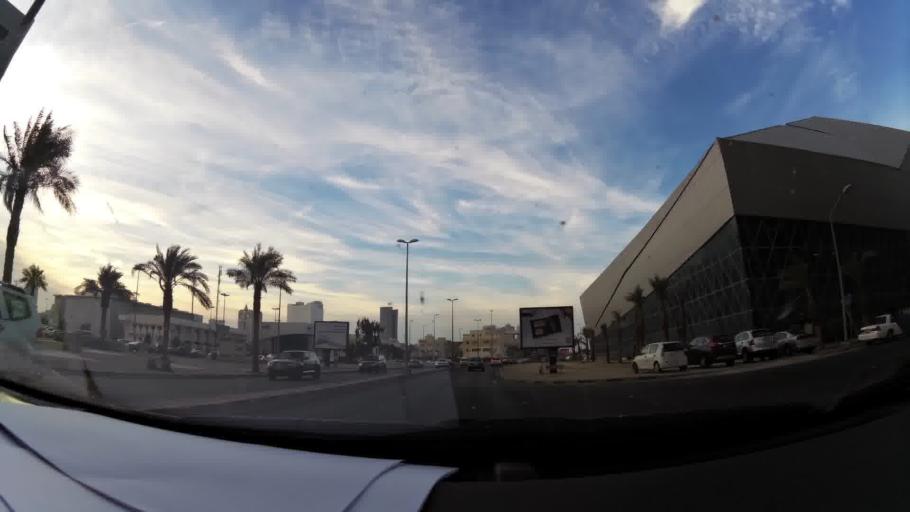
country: KW
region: Muhafazat Hawalli
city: As Salimiyah
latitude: 29.3394
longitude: 48.0847
